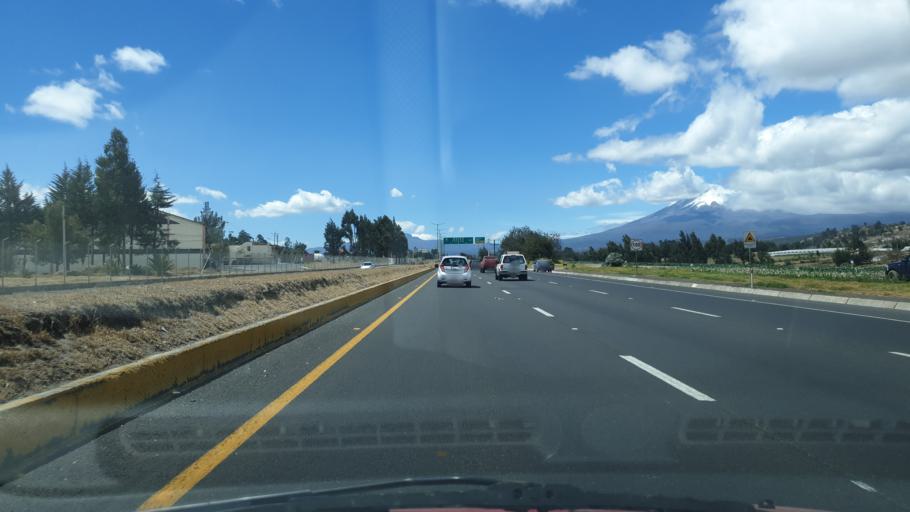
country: EC
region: Cotopaxi
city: Saquisili
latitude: -0.8581
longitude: -78.6223
